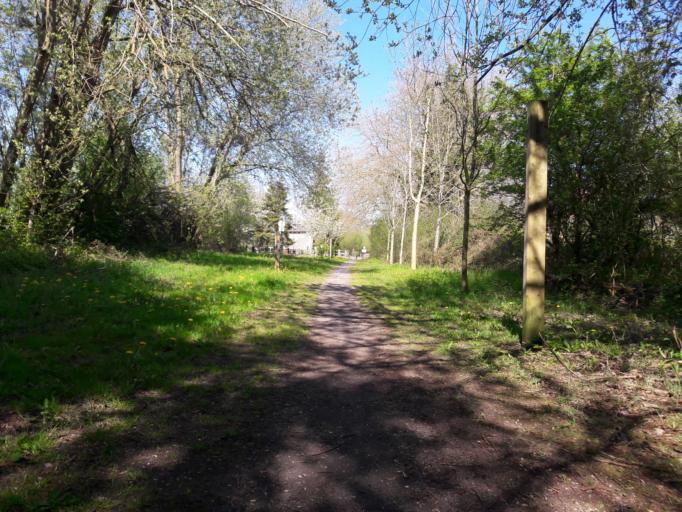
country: FR
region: Nord-Pas-de-Calais
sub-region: Departement du Nord
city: Sains-du-Nord
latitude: 50.1717
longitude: 4.0781
